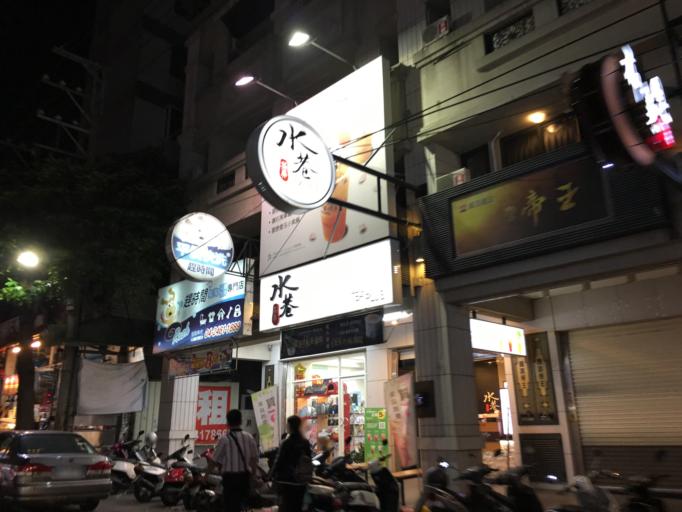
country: TW
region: Taiwan
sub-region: Taichung City
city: Taichung
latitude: 24.1871
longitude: 120.6206
